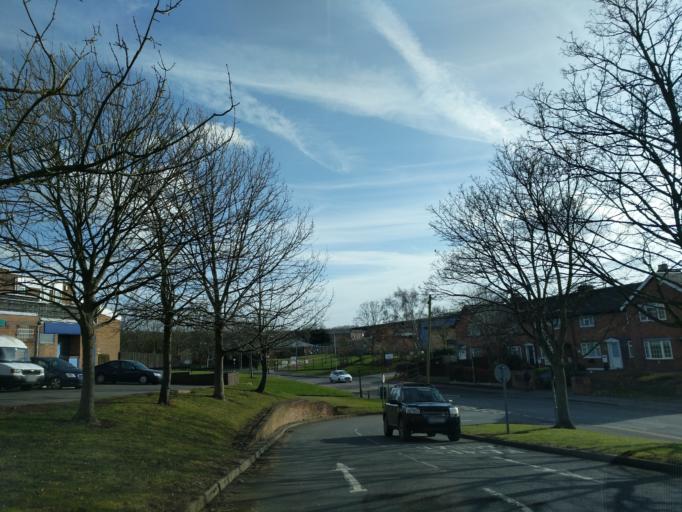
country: GB
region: England
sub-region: Nottinghamshire
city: Cotgrave
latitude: 52.9103
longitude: -1.0381
